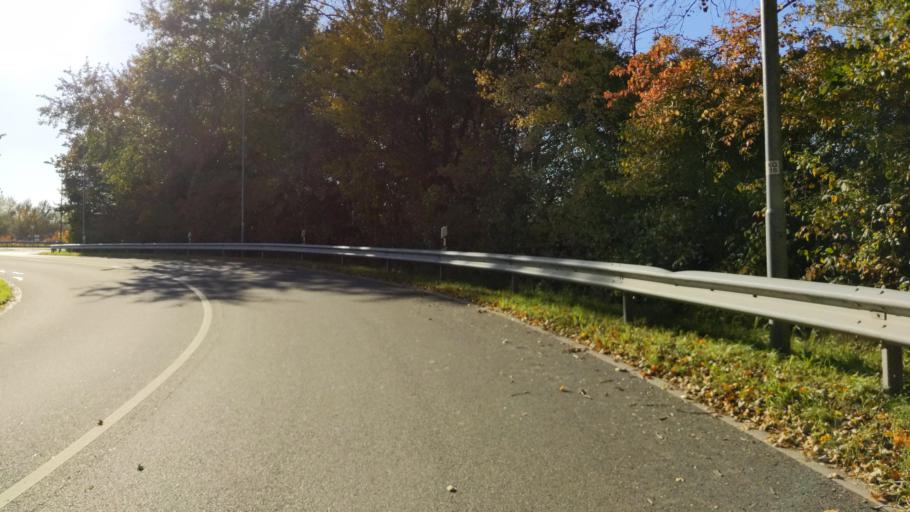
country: DE
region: Schleswig-Holstein
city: Ratekau
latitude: 53.8997
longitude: 10.7637
